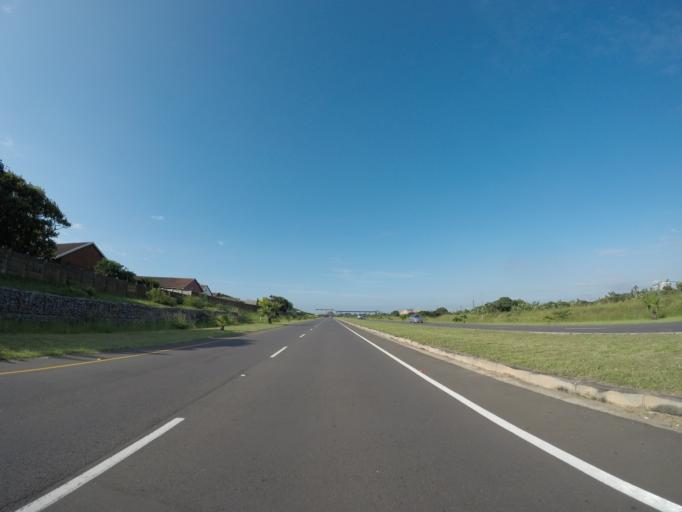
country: ZA
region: KwaZulu-Natal
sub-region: uThungulu District Municipality
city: Richards Bay
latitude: -28.7612
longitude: 32.0506
